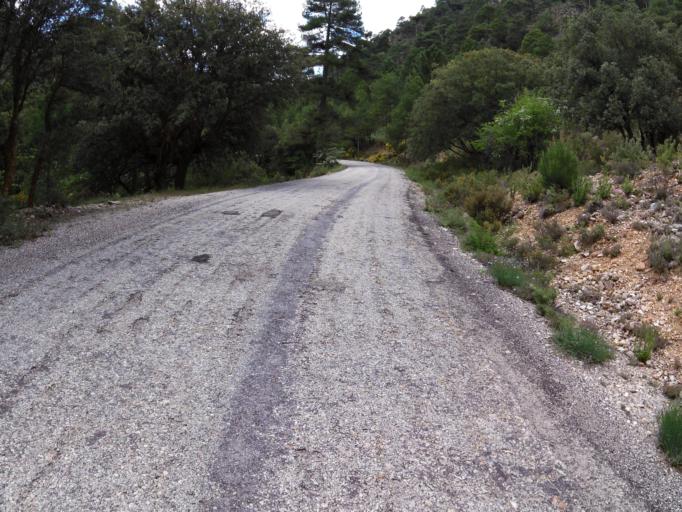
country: ES
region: Castille-La Mancha
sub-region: Provincia de Albacete
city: Paterna del Madera
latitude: 38.5777
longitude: -2.3518
